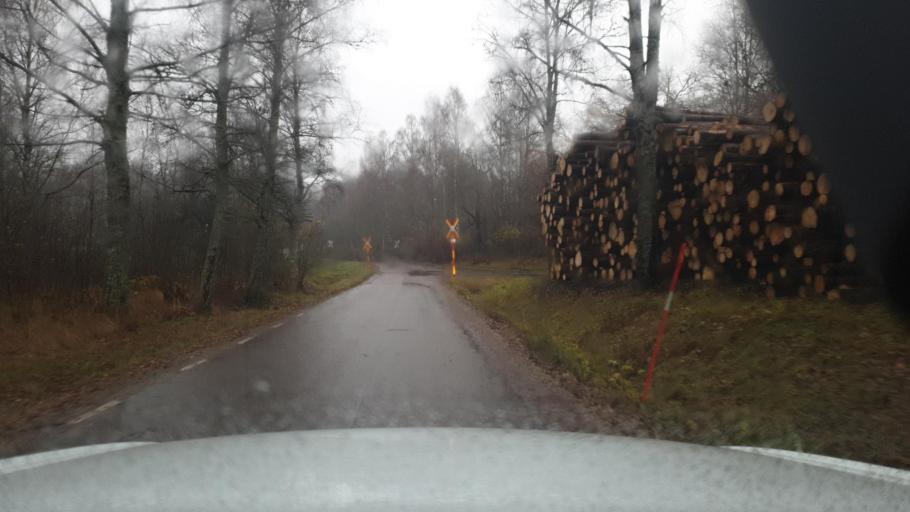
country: SE
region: Vaermland
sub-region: Sunne Kommun
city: Sunne
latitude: 59.7955
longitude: 13.1269
